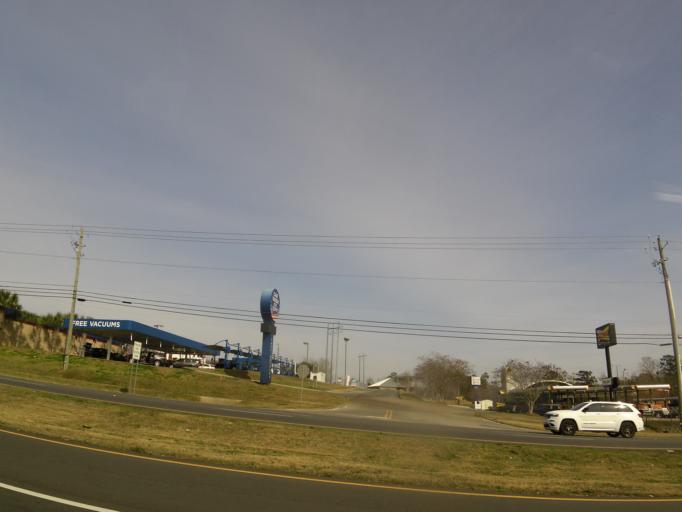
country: US
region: Alabama
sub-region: Houston County
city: Dothan
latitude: 31.2643
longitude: -85.4411
